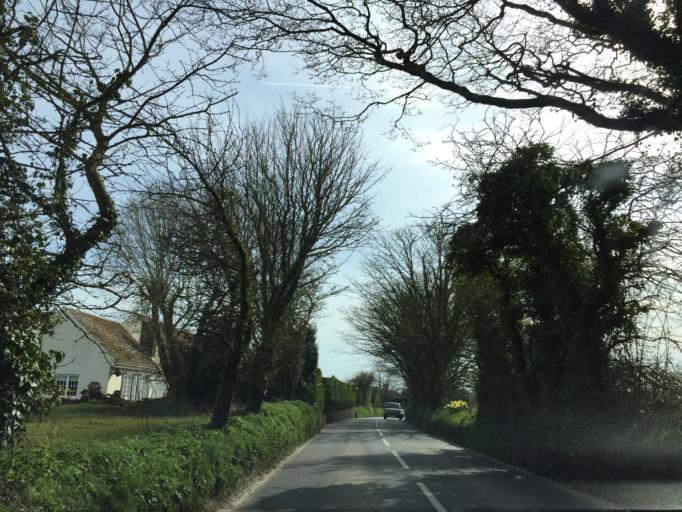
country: JE
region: St Helier
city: Saint Helier
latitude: 49.2329
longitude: -2.0845
